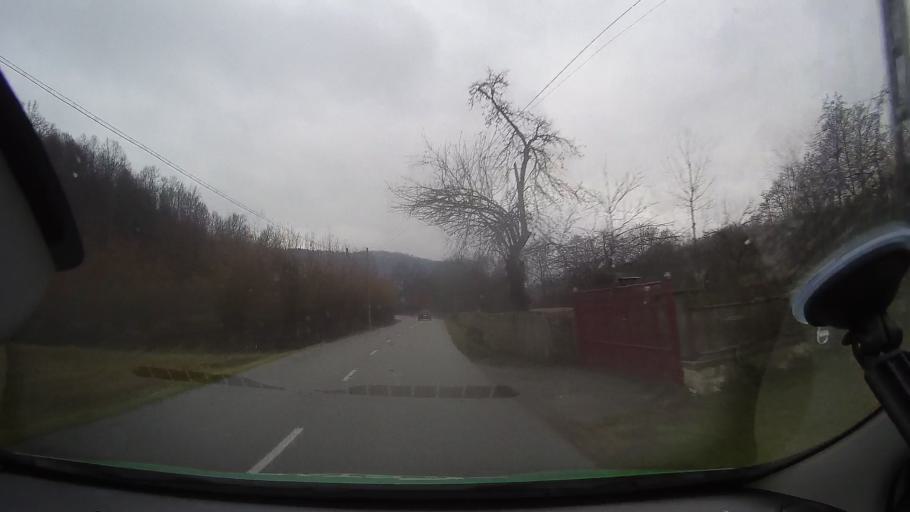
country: RO
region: Hunedoara
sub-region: Comuna Tomesti
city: Tomesti
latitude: 46.2004
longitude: 22.6589
